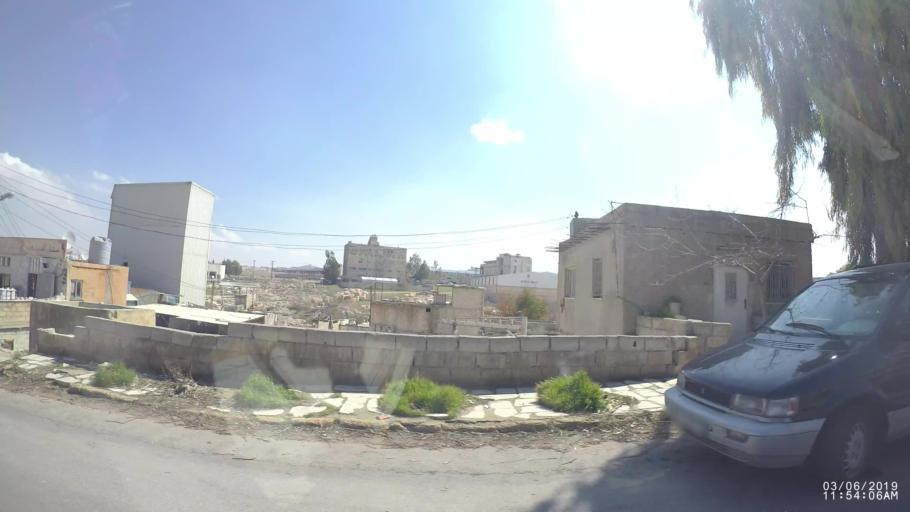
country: JO
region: Zarqa
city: Russeifa
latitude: 31.9872
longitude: 36.0072
